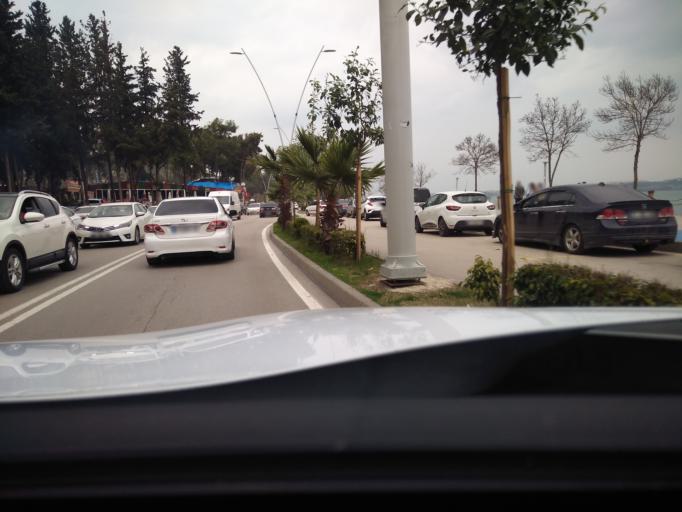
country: TR
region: Adana
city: Adana
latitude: 37.0513
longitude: 35.3067
